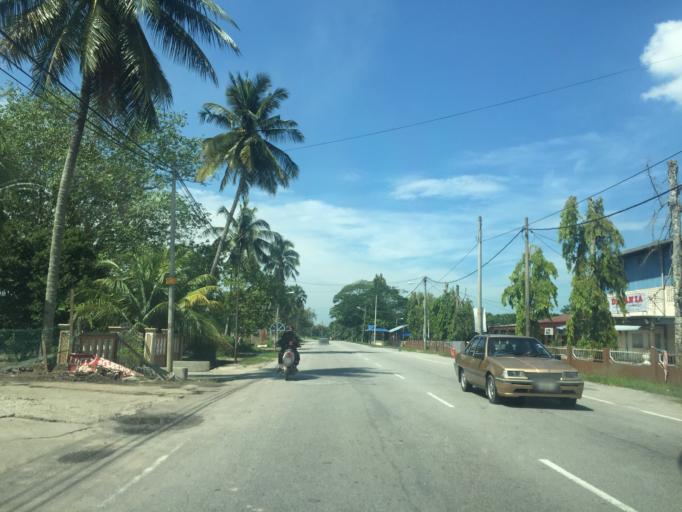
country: MY
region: Penang
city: Tasek Glugor
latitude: 5.4887
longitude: 100.4695
